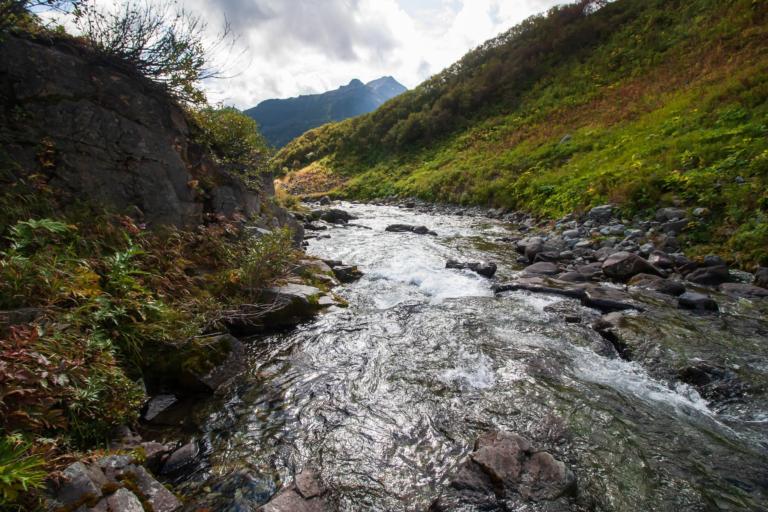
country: RU
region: Kamtsjatka
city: Yelizovo
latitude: 53.8324
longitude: 158.2883
